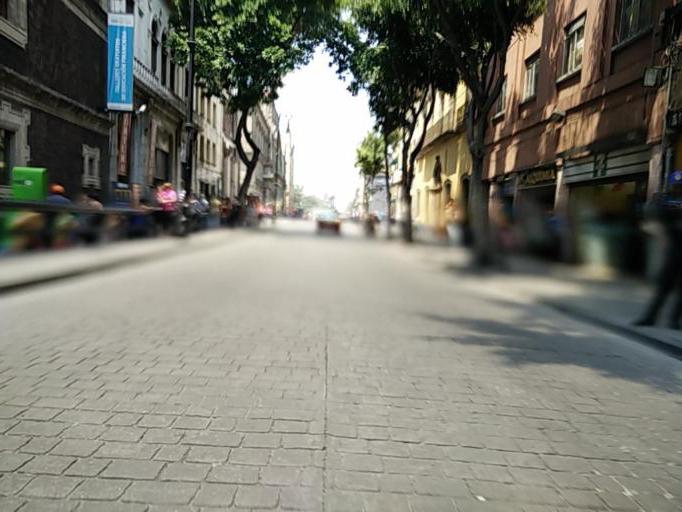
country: MX
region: Mexico City
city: Cuauhtemoc
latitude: 19.4357
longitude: -99.1383
